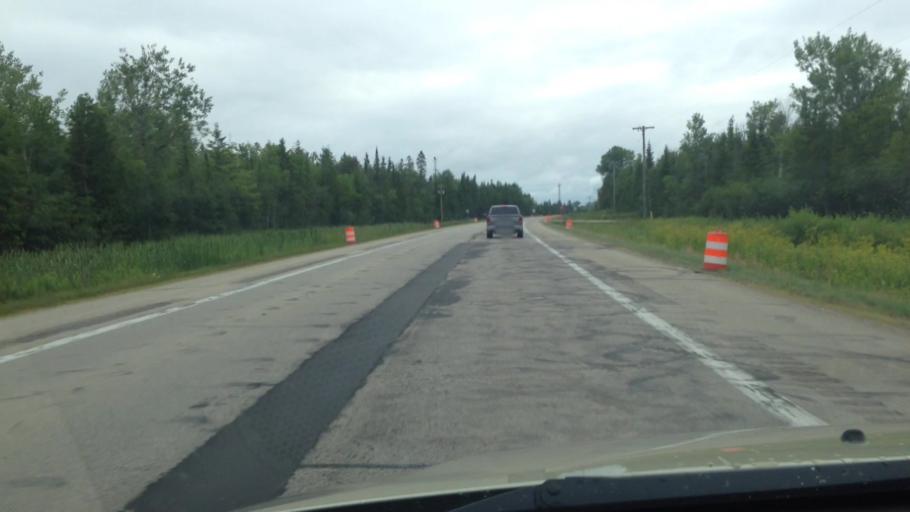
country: US
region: Michigan
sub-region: Delta County
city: Escanaba
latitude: 45.6309
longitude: -87.2045
